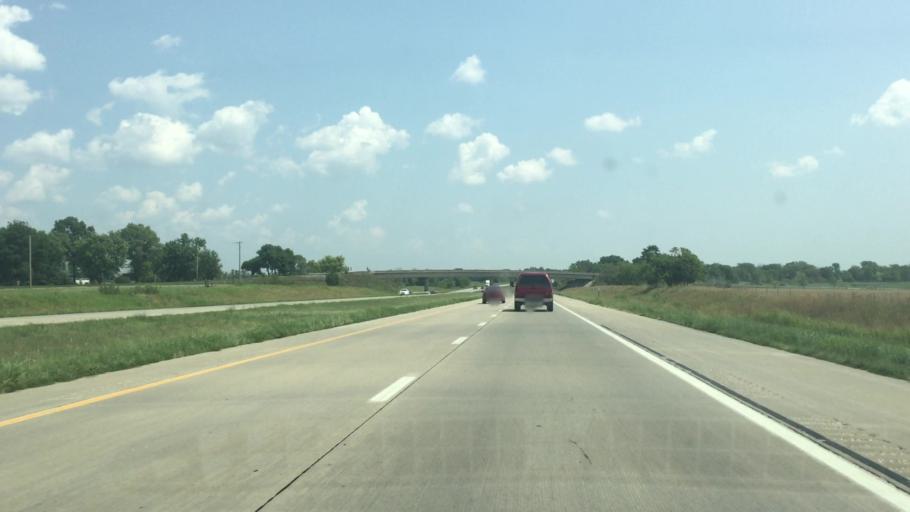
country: US
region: Kansas
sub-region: Franklin County
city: Wellsville
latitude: 38.6929
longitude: -95.1075
